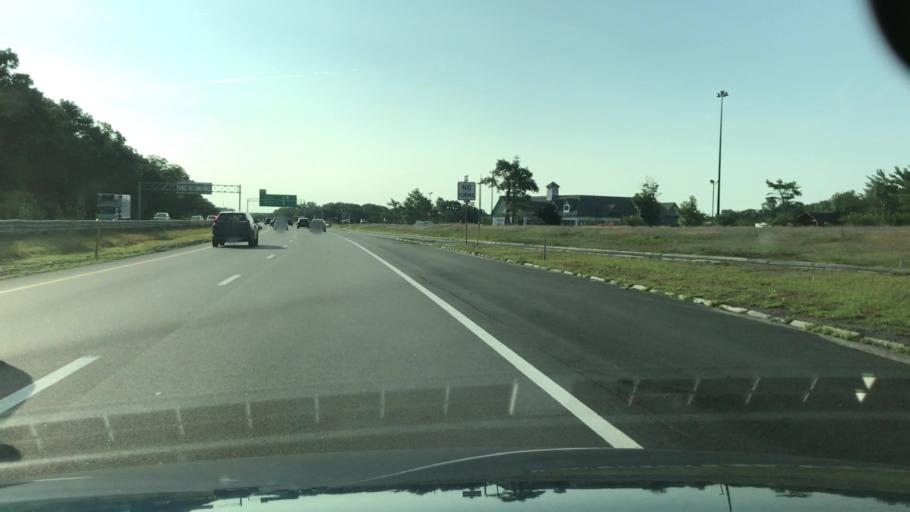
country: US
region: Massachusetts
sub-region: Plymouth County
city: Plymouth
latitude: 41.9373
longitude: -70.6632
